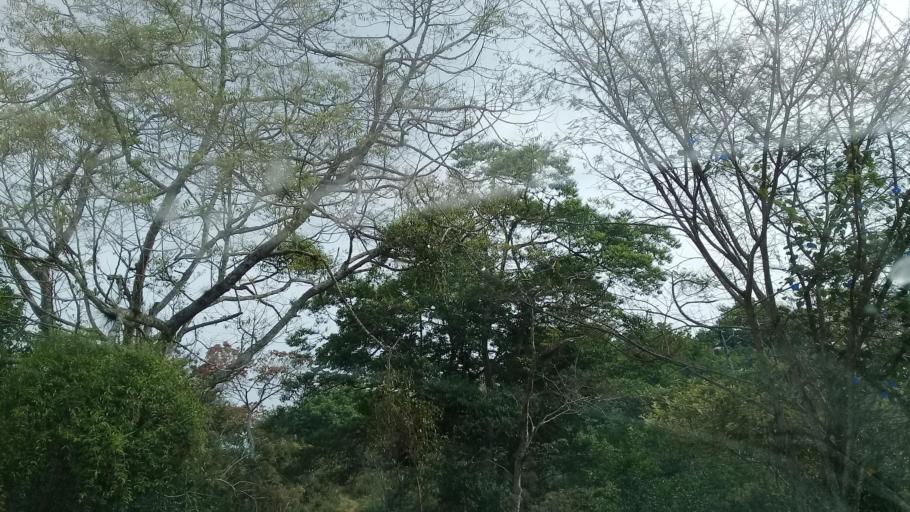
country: MX
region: Veracruz
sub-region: Xalapa
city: Fraccionamiento las Fuentes
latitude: 19.4950
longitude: -96.8949
